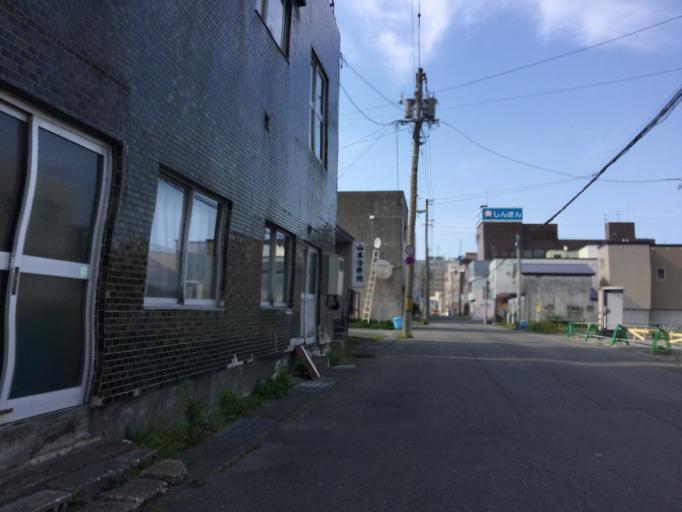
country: JP
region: Hokkaido
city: Wakkanai
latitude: 45.4149
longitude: 141.6746
